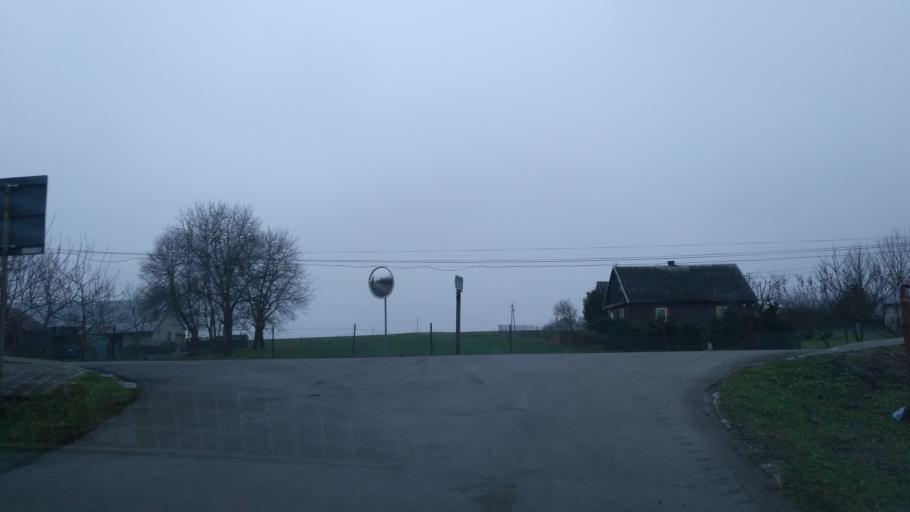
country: PL
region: Subcarpathian Voivodeship
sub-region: Powiat przeworski
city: Zarzecze
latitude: 49.9730
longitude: 22.5532
